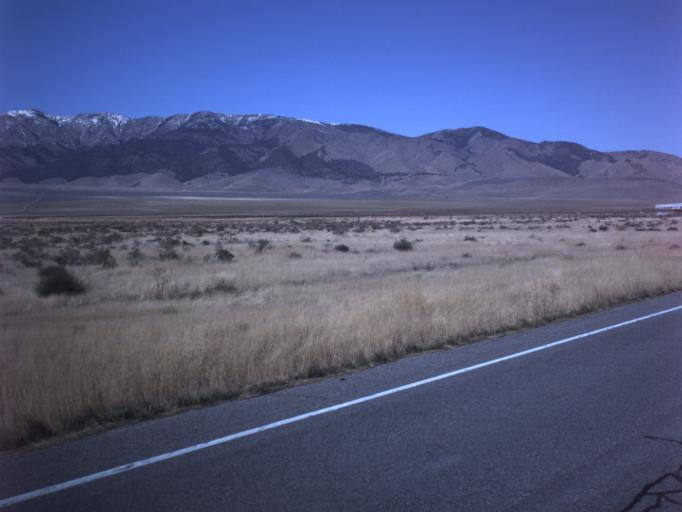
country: US
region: Utah
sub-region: Tooele County
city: Grantsville
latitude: 40.6085
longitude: -112.4908
